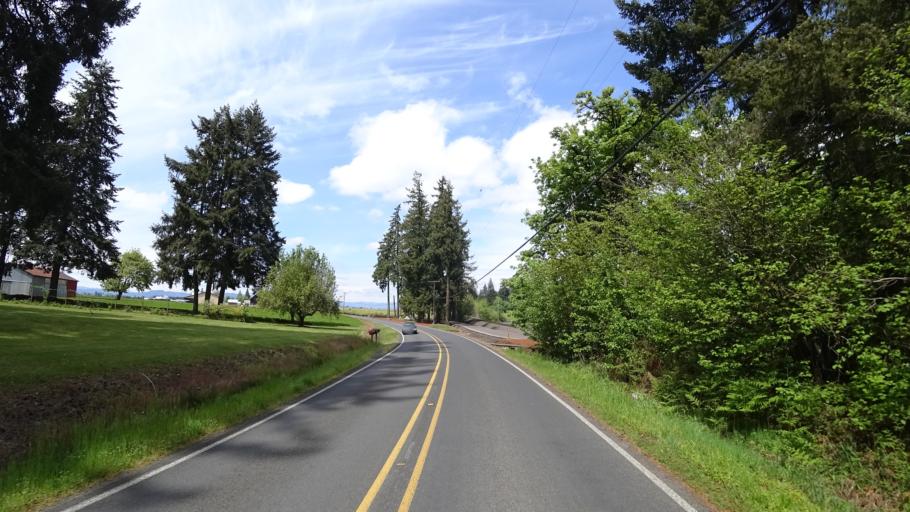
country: US
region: Oregon
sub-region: Washington County
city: Hillsboro
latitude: 45.5435
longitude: -123.0058
